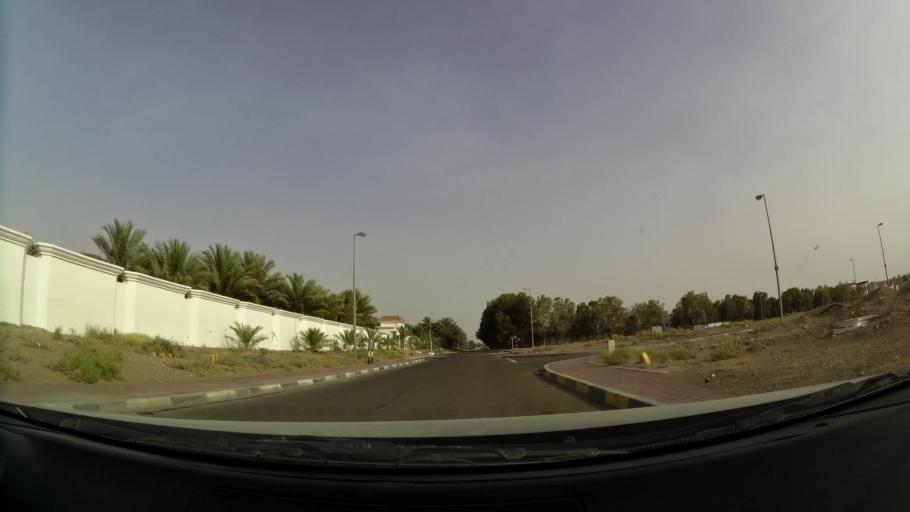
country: AE
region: Abu Dhabi
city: Al Ain
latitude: 24.2213
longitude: 55.6488
